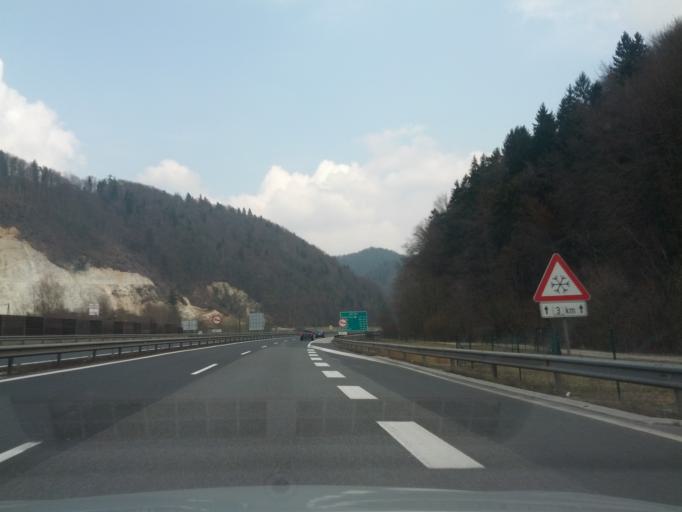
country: SI
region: Lukovica
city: Lukovica pri Domzalah
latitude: 46.1707
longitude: 14.6996
